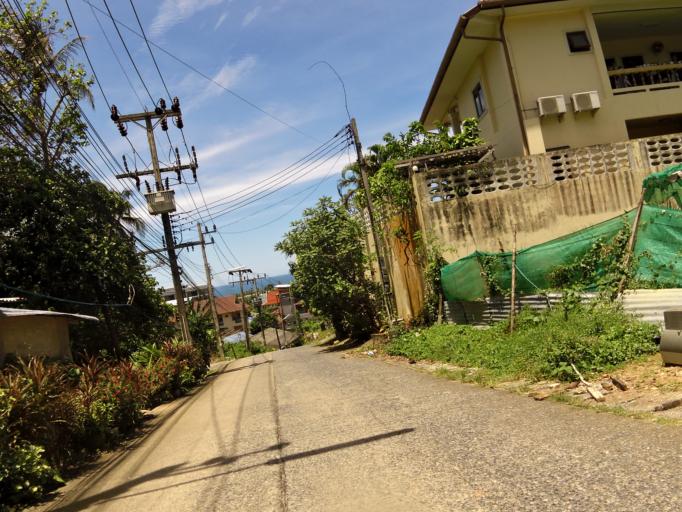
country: TH
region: Phuket
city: Ban Karon
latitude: 7.8493
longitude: 98.3021
